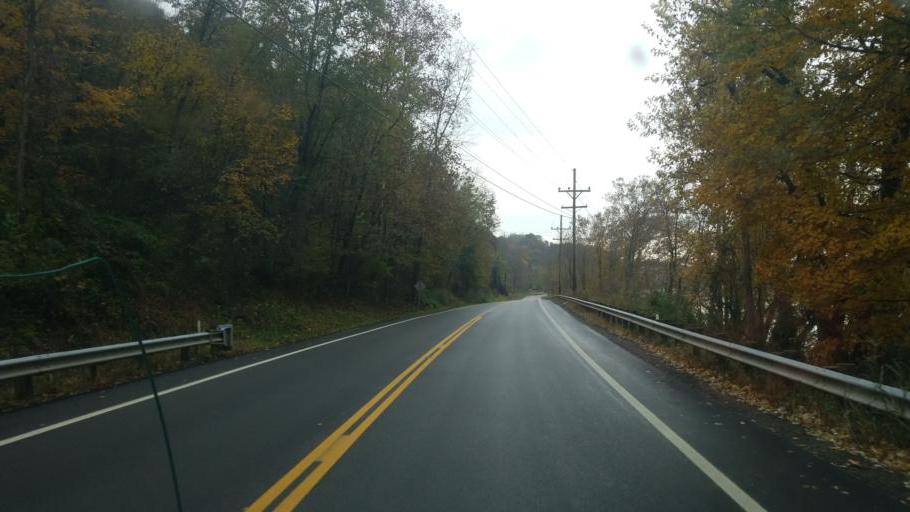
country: US
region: Ohio
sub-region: Washington County
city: Beverly
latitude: 39.5668
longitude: -81.5781
